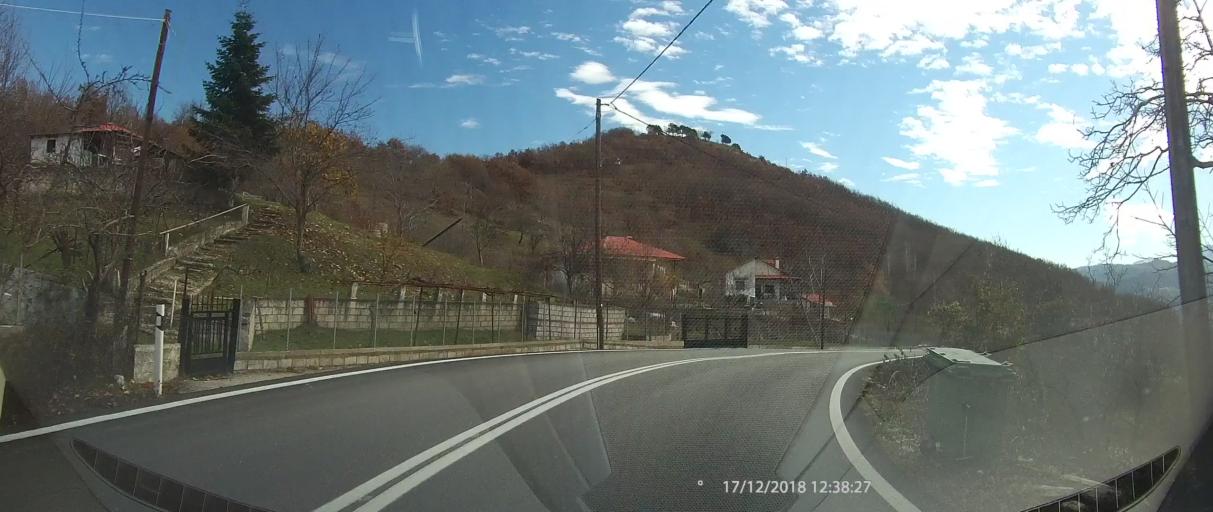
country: GR
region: Epirus
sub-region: Nomos Ioanninon
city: Metsovo
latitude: 39.8095
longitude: 21.3466
